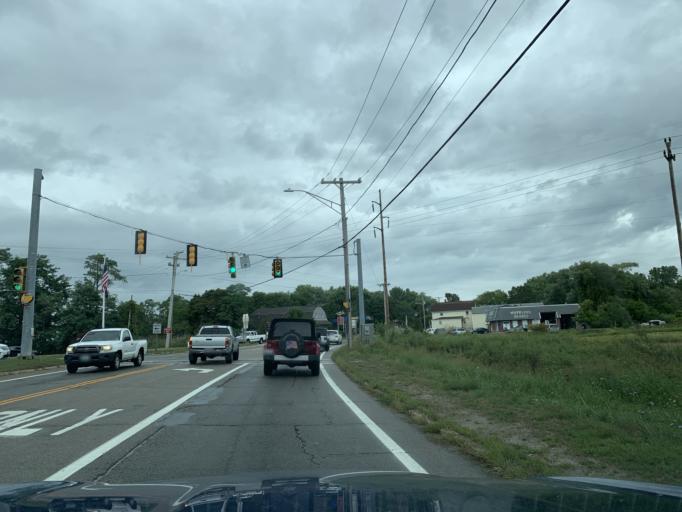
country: US
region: Rhode Island
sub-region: Bristol County
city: Warren
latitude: 41.7330
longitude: -71.2732
